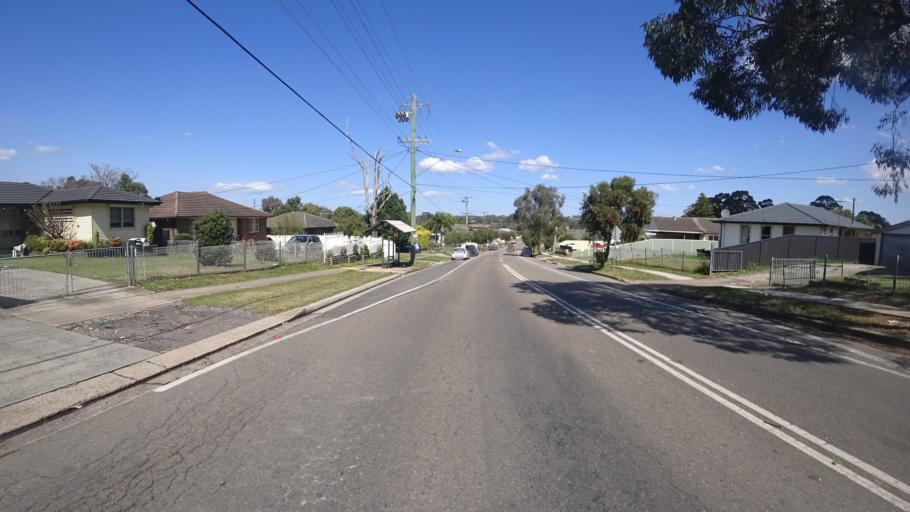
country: AU
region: New South Wales
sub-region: Liverpool
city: Miller
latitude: -33.9122
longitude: 150.8948
